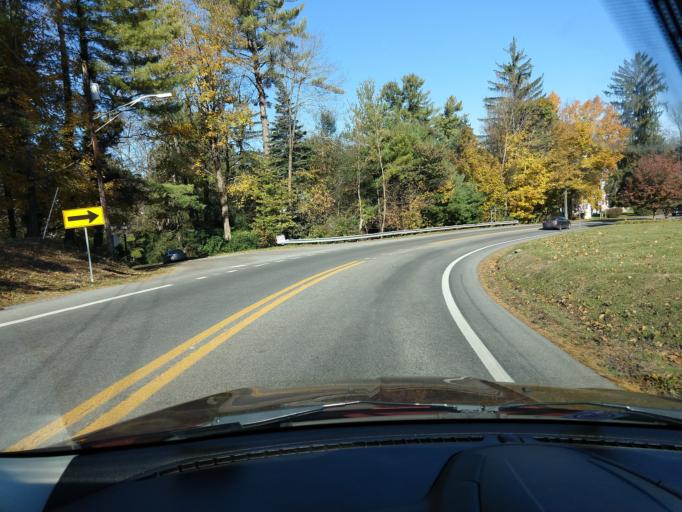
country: US
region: West Virginia
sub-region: Greenbrier County
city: Lewisburg
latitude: 37.7980
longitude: -80.4485
